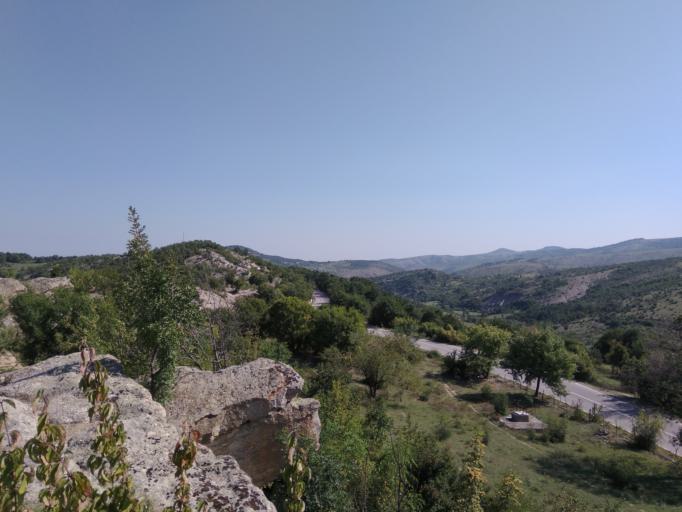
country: BG
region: Kurdzhali
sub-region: Obshtina Krumovgrad
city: Krumovgrad
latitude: 41.5111
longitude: 25.6638
